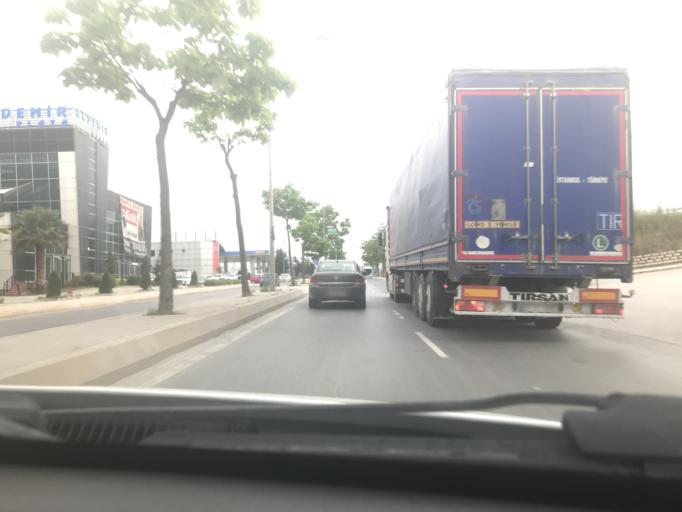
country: TR
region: Istanbul
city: Sultanbeyli
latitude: 40.9275
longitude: 29.3191
